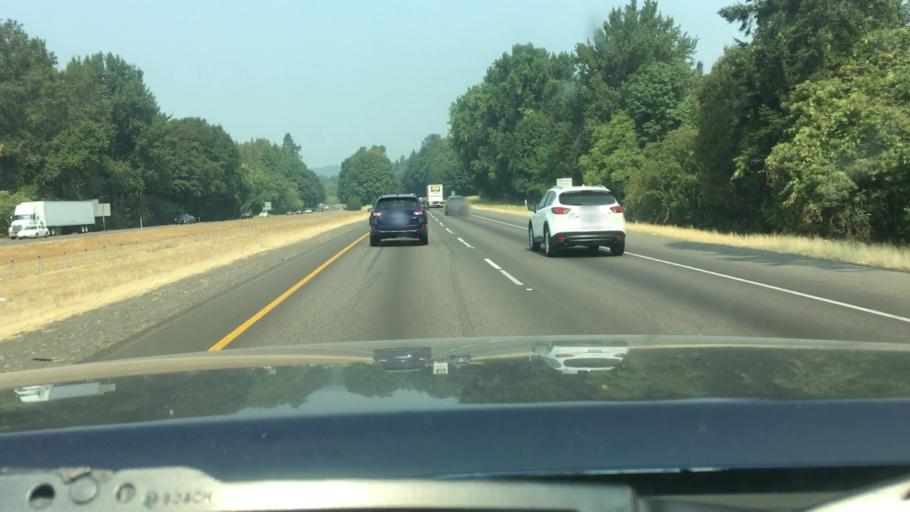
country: US
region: Oregon
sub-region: Clackamas County
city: West Linn
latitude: 45.3536
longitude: -122.6623
